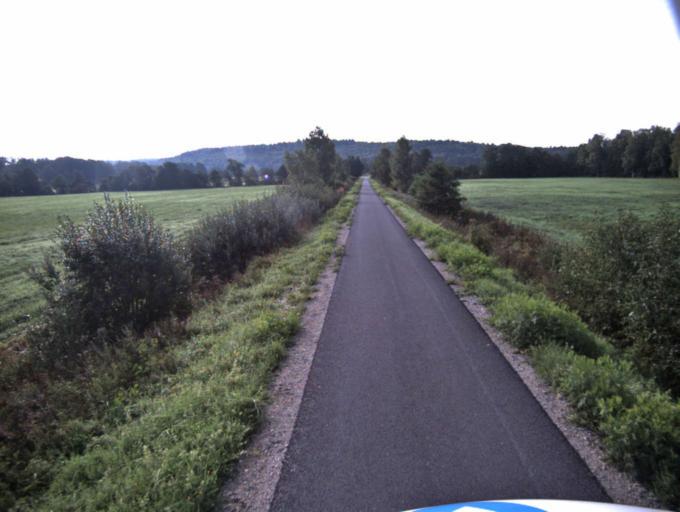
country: SE
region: Vaestra Goetaland
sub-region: Ulricehamns Kommun
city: Ulricehamn
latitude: 57.7376
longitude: 13.4044
